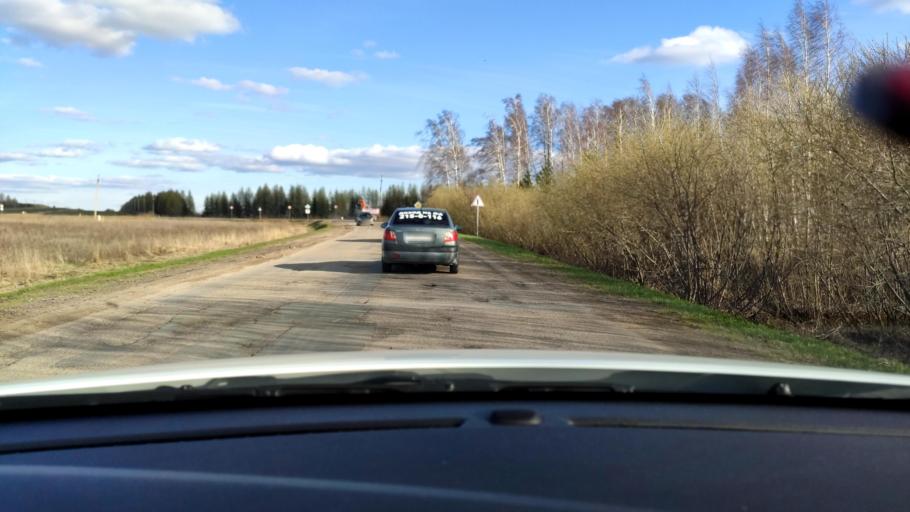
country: RU
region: Tatarstan
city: Vysokaya Gora
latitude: 55.8944
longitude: 49.3336
